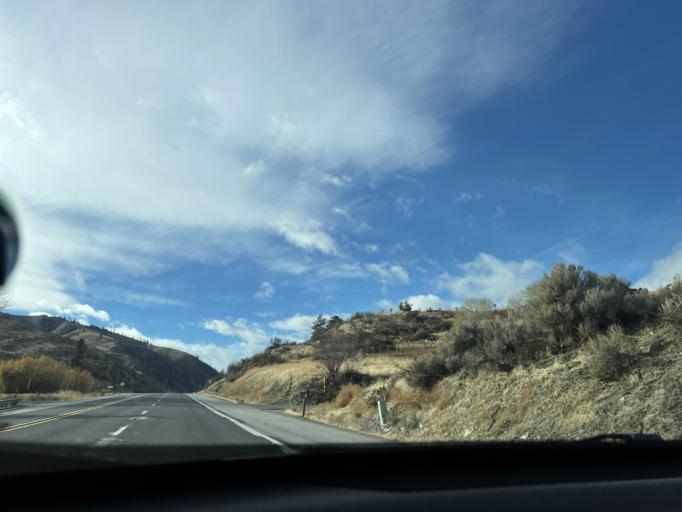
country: US
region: Washington
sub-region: Chelan County
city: Manson
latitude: 47.8397
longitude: -120.1055
